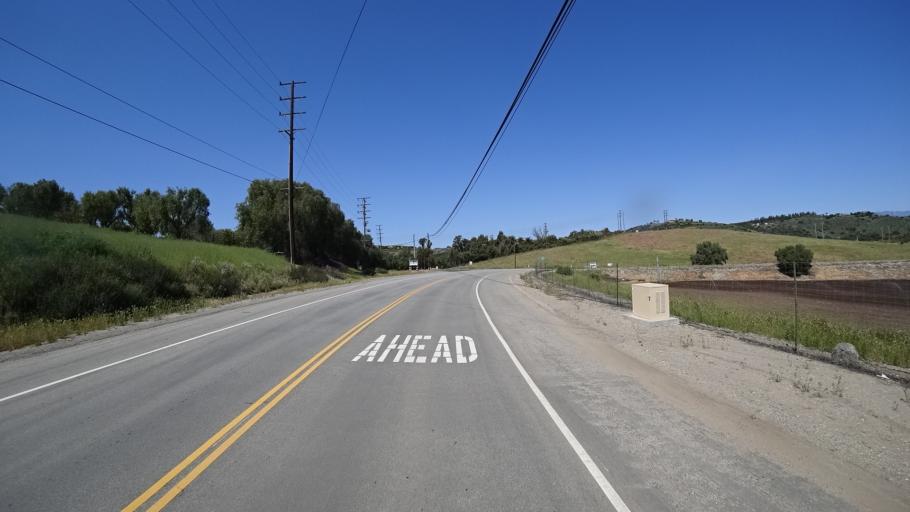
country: US
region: California
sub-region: Ventura County
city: Moorpark
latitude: 34.2499
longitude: -118.8636
